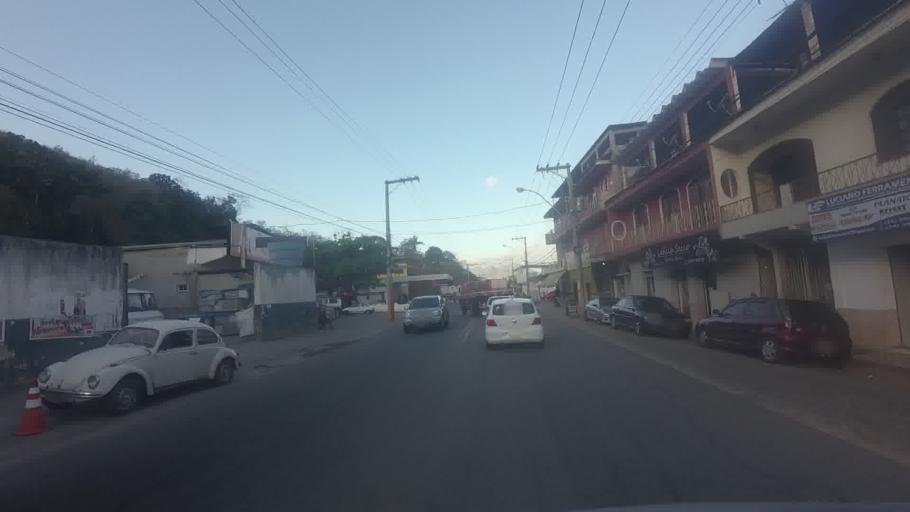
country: BR
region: Espirito Santo
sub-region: Cachoeiro De Itapemirim
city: Cachoeiro de Itapemirim
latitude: -20.8462
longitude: -41.1359
